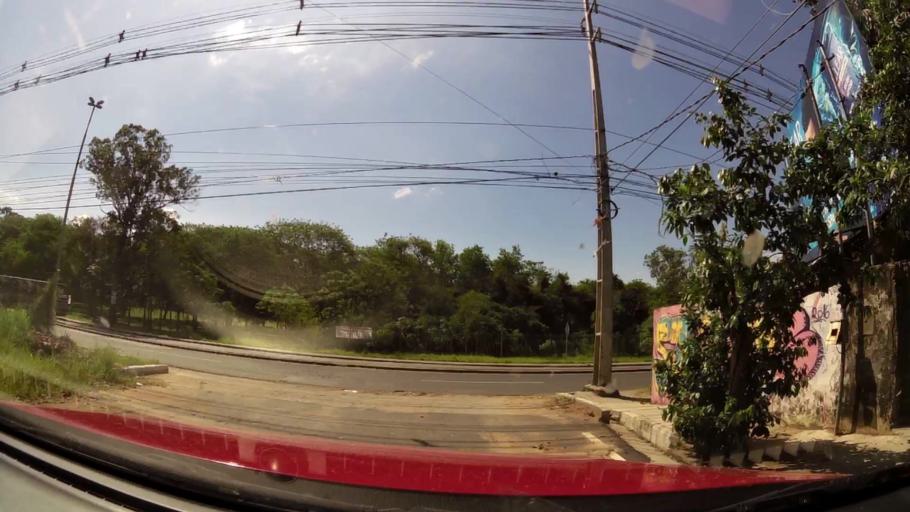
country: PY
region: Asuncion
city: Asuncion
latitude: -25.2557
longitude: -57.5644
